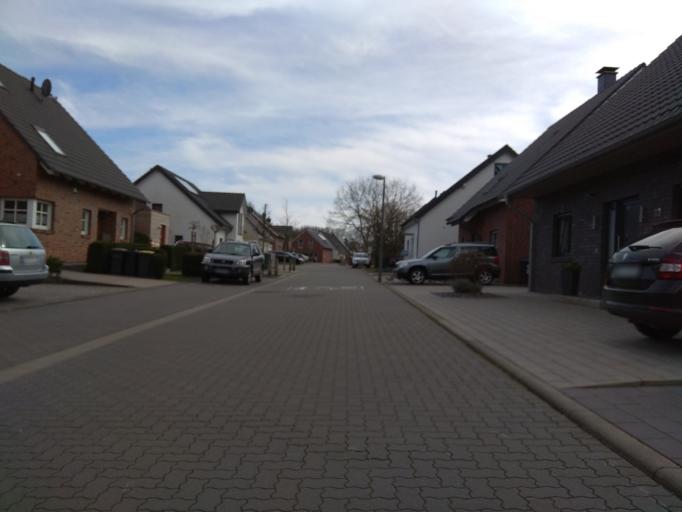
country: DE
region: North Rhine-Westphalia
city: Marl
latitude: 51.6423
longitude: 7.0811
